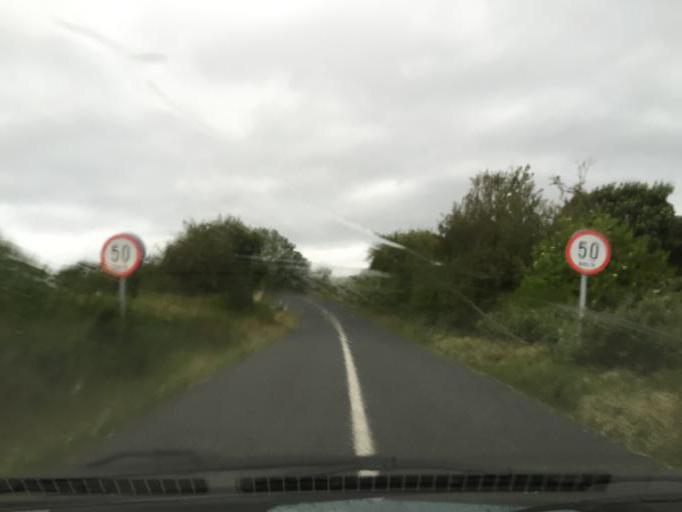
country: IE
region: Connaught
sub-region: Sligo
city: Strandhill
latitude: 54.2574
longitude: -8.5970
